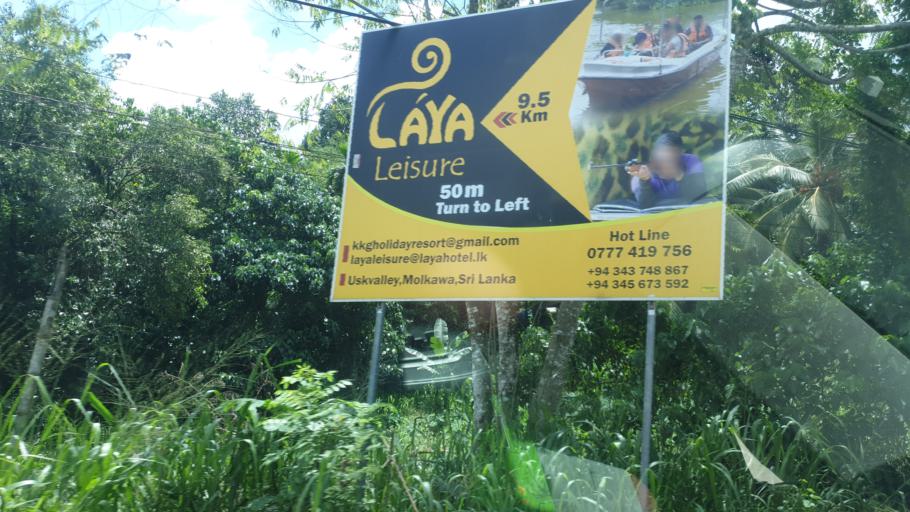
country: LK
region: Western
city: Horawala Junction
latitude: 6.5248
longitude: 80.2128
